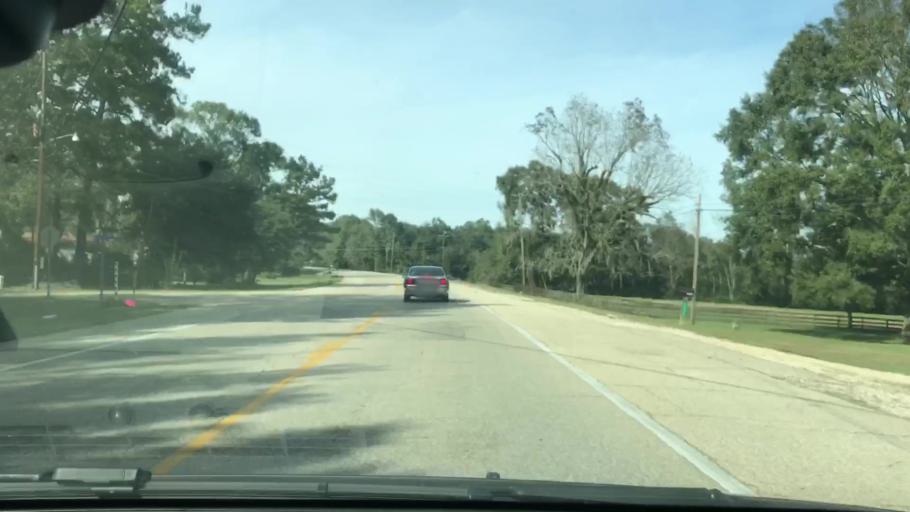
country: US
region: Louisiana
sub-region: Saint Tammany Parish
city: Pearl River
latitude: 30.4571
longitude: -89.8029
